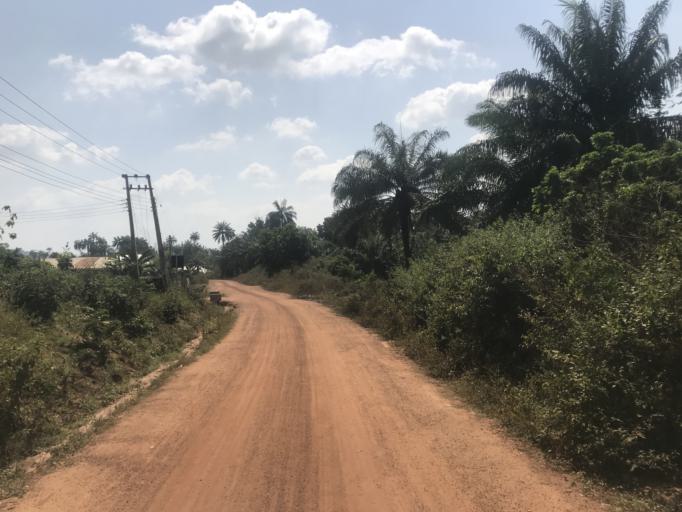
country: NG
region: Osun
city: Iragbiji
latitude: 7.8857
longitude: 4.7007
